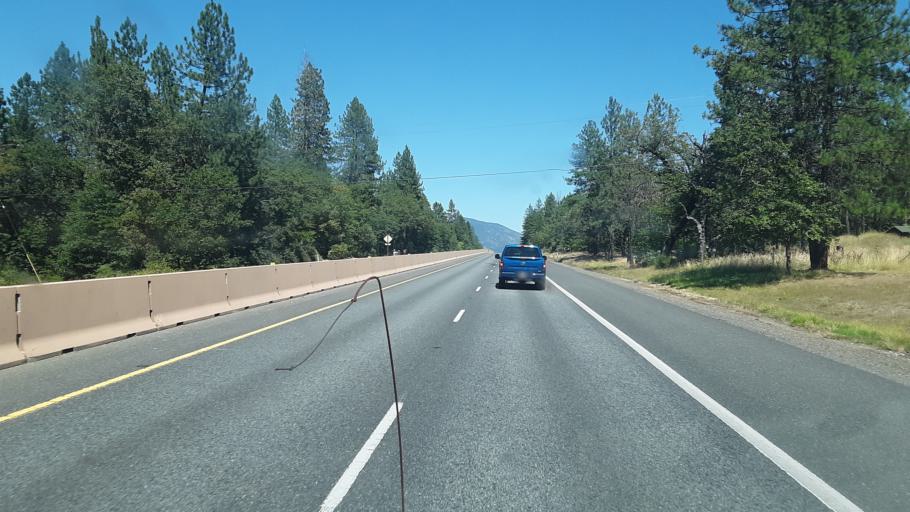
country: US
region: Oregon
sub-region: Josephine County
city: Redwood
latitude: 42.4137
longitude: -123.4022
